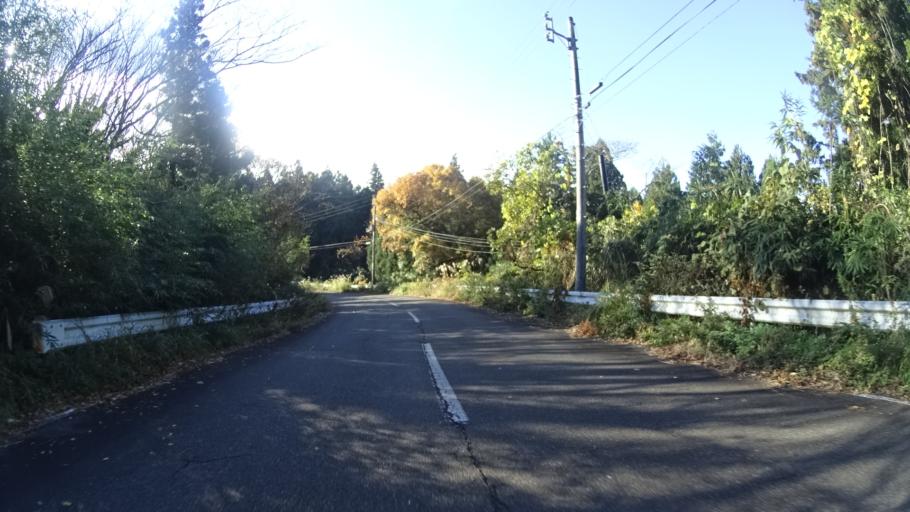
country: JP
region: Niigata
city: Yoshida-kasugacho
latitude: 37.6610
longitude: 138.8129
